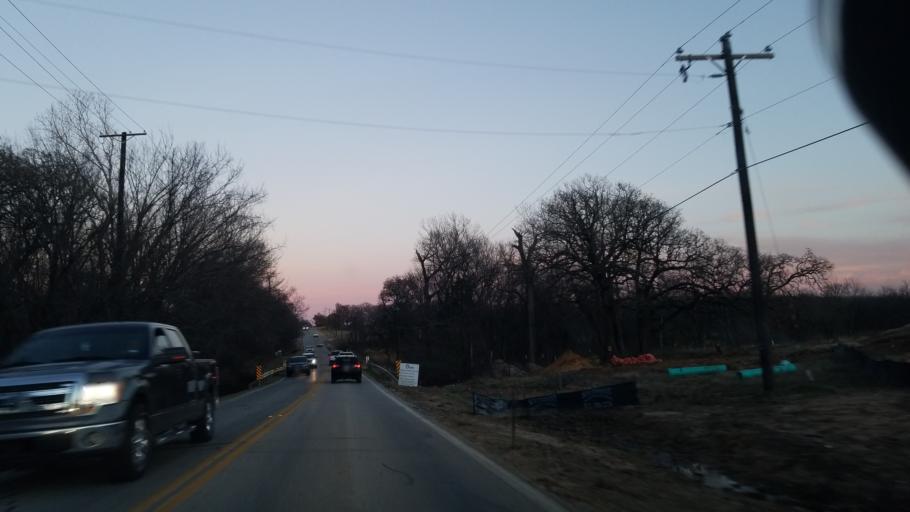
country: US
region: Texas
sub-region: Denton County
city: Denton
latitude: 33.1615
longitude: -97.1263
